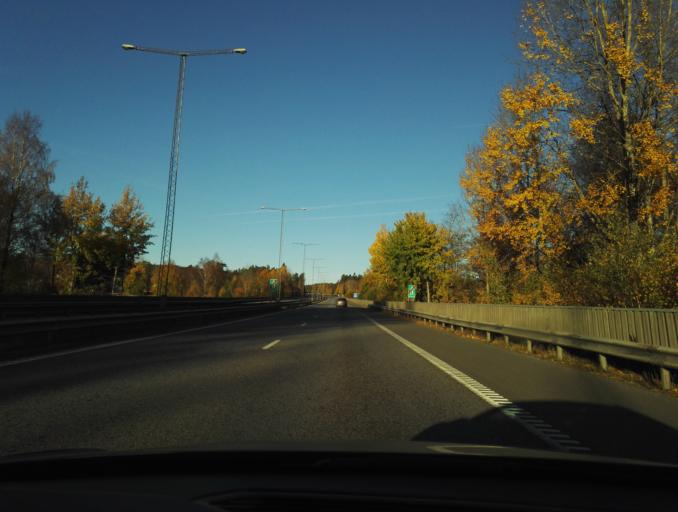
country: SE
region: Kronoberg
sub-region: Vaxjo Kommun
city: Vaexjoe
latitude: 56.8941
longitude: 14.7415
